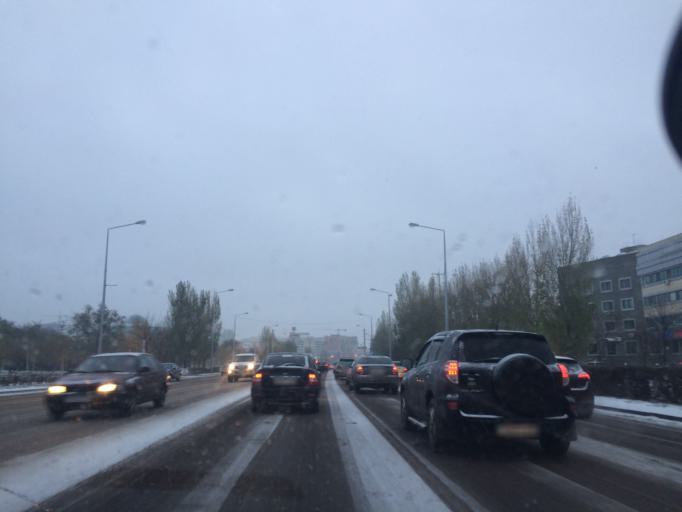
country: KZ
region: Astana Qalasy
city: Astana
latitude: 51.1495
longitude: 71.4125
